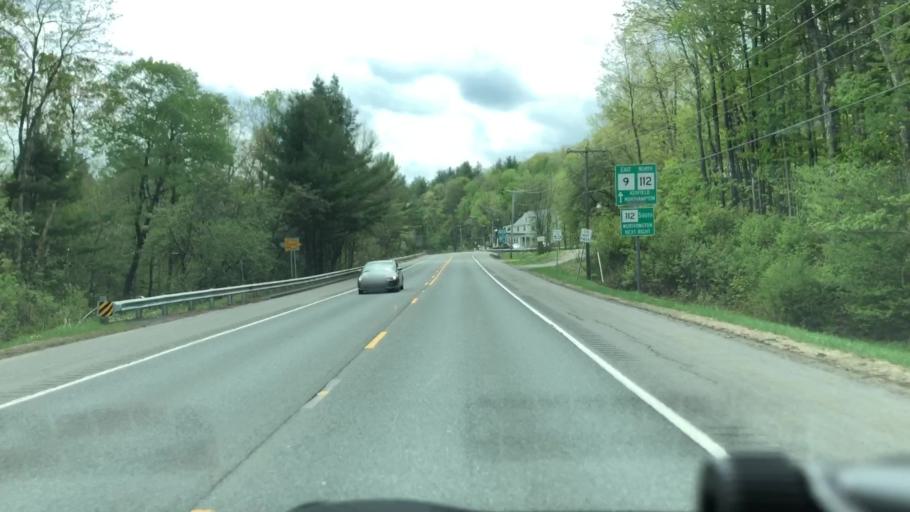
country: US
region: Massachusetts
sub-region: Hampshire County
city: Chesterfield
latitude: 42.4660
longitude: -72.9059
